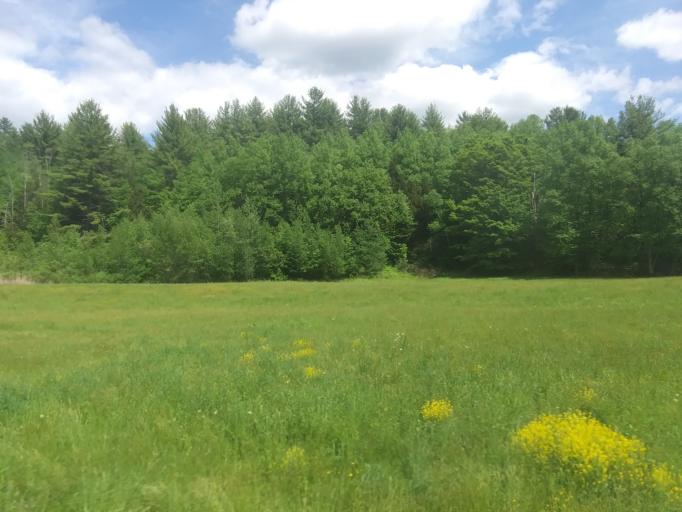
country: US
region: Massachusetts
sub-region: Franklin County
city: Buckland
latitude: 42.5726
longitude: -72.8109
